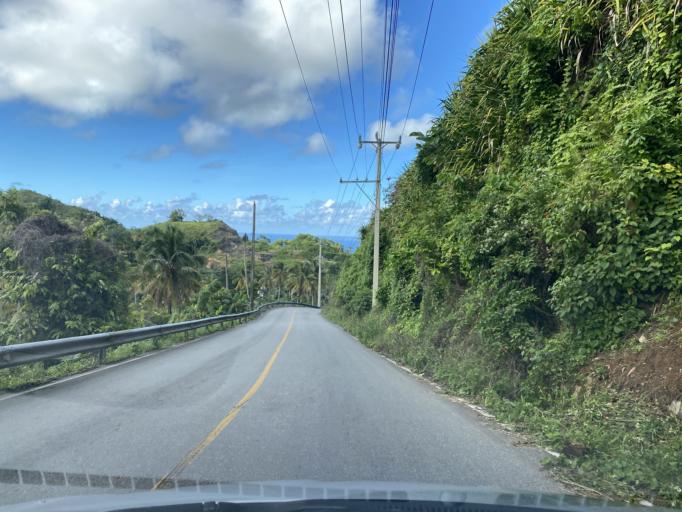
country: DO
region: Samana
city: Las Terrenas
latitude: 19.2781
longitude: -69.5534
